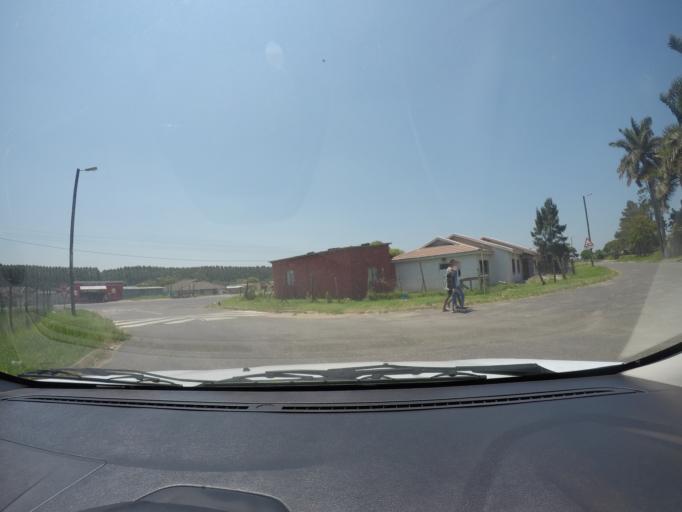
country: ZA
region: KwaZulu-Natal
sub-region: uThungulu District Municipality
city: eSikhawini
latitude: -28.8879
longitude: 31.8832
